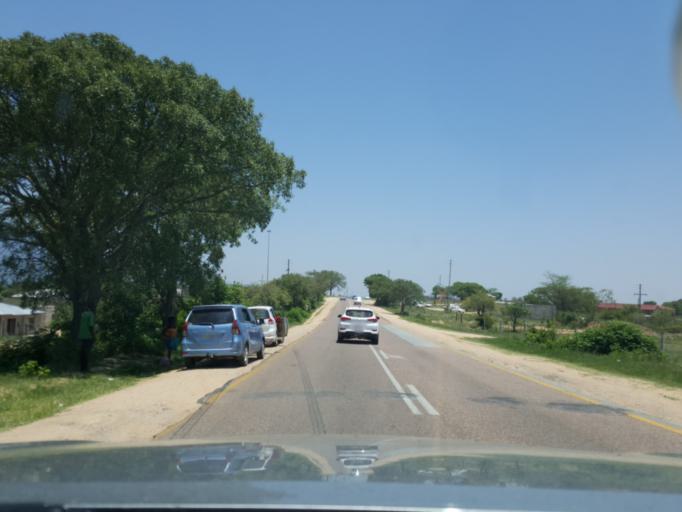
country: ZA
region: Limpopo
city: Thulamahashi
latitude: -24.5934
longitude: 31.0435
